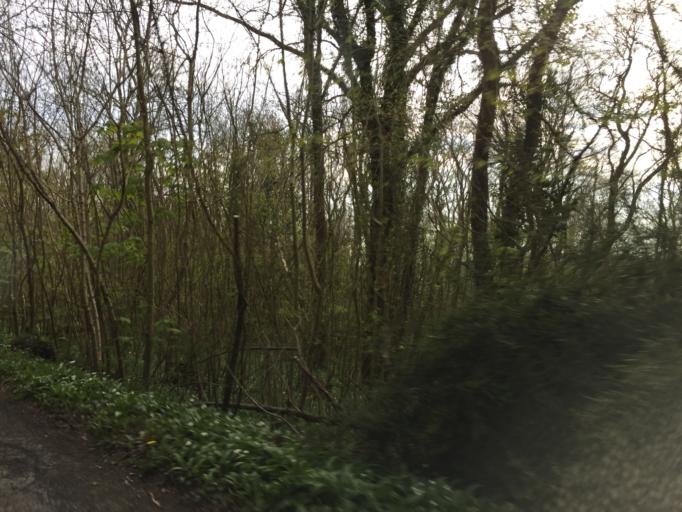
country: GB
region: Wales
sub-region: Cardiff
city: Radyr
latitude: 51.5444
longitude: -3.2354
